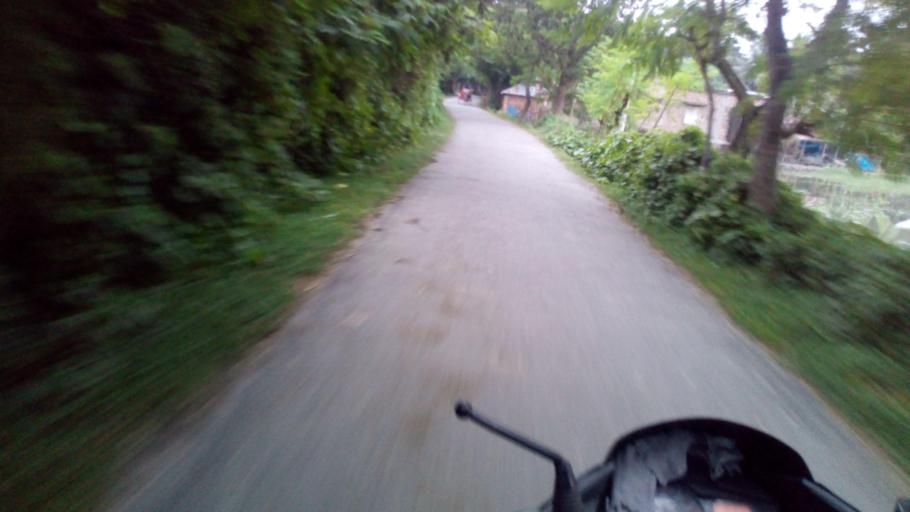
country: BD
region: Khulna
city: Phultala
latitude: 22.7617
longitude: 89.4086
